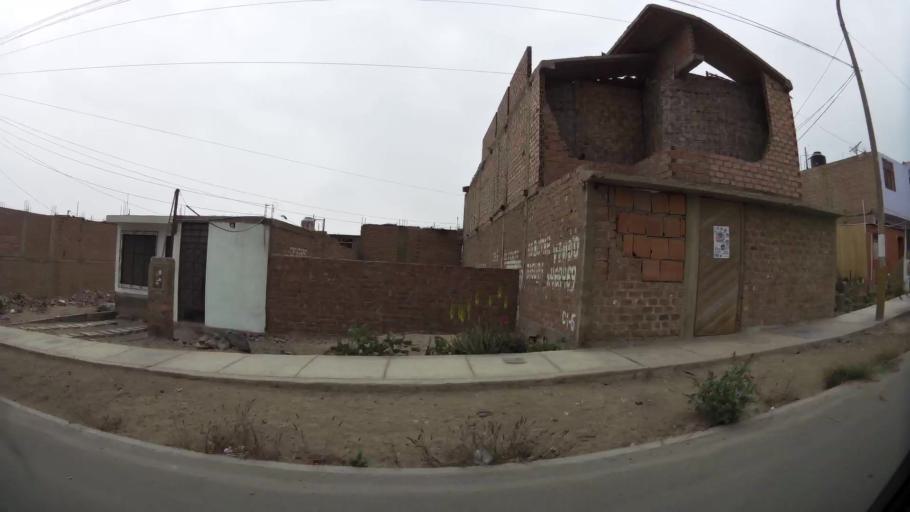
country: PE
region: Lima
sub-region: Lima
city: Santa Rosa
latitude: -11.7911
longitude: -77.1566
